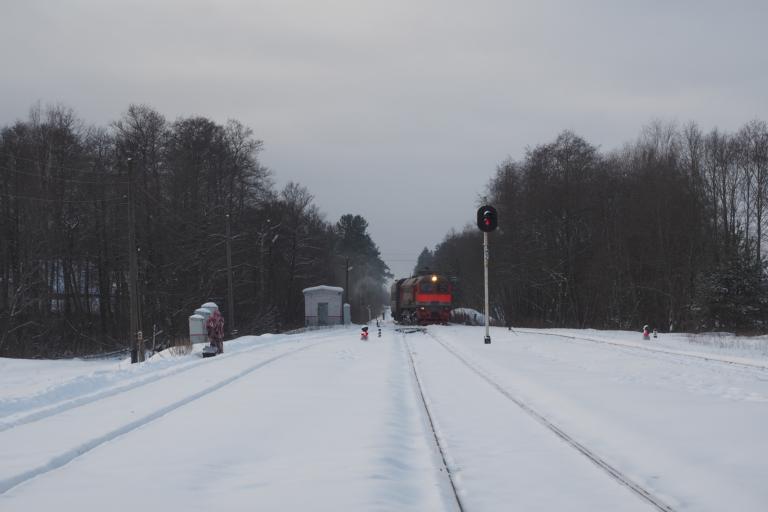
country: RU
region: Tverskaya
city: Ves'yegonsk
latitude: 58.6512
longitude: 37.2548
